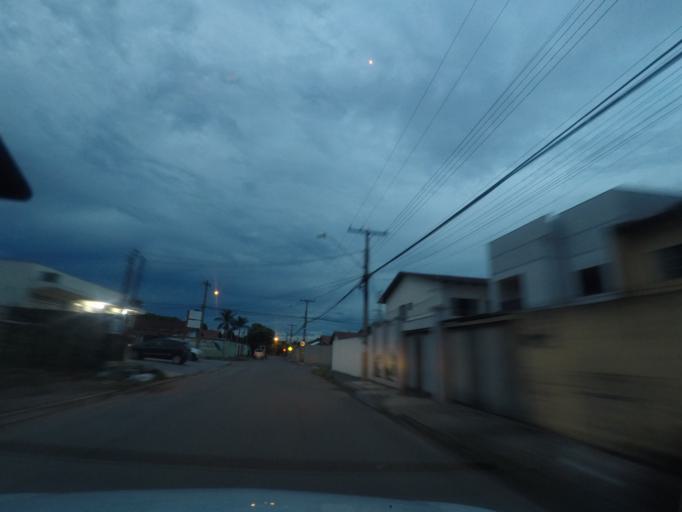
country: BR
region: Goias
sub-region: Goiania
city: Goiania
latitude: -16.7187
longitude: -49.3016
